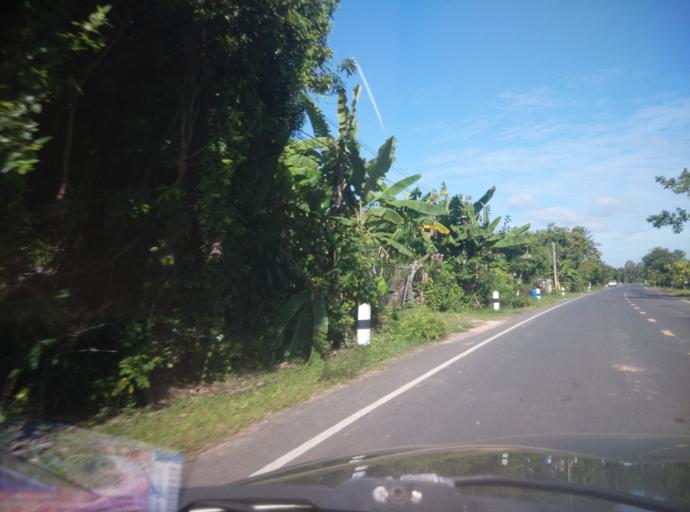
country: TH
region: Sisaket
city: Uthumphon Phisai
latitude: 15.1194
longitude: 104.2235
